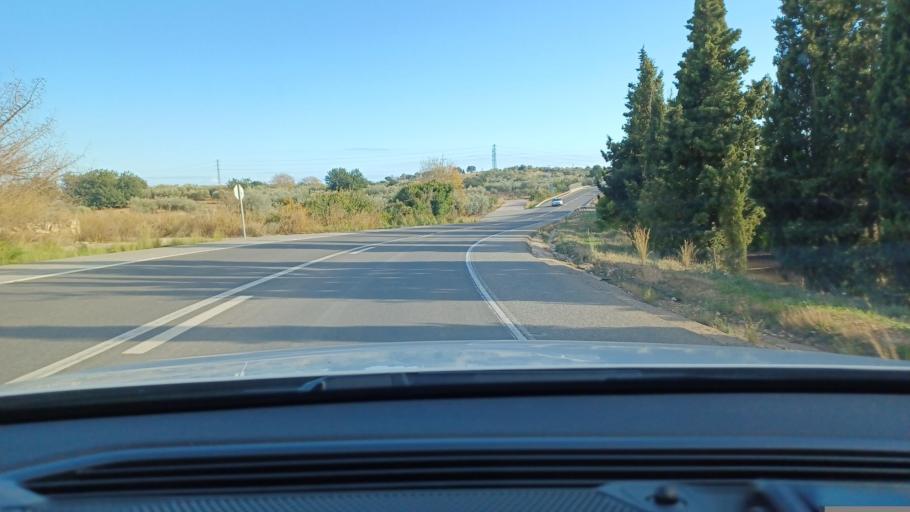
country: ES
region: Catalonia
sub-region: Provincia de Tarragona
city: Masdenverge
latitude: 40.7080
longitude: 0.5454
